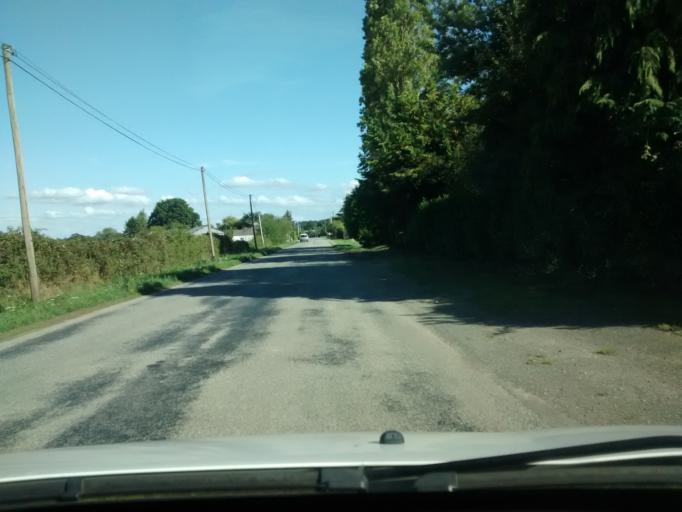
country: FR
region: Brittany
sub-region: Departement d'Ille-et-Vilaine
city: Nouvoitou
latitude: 48.0727
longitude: -1.5711
